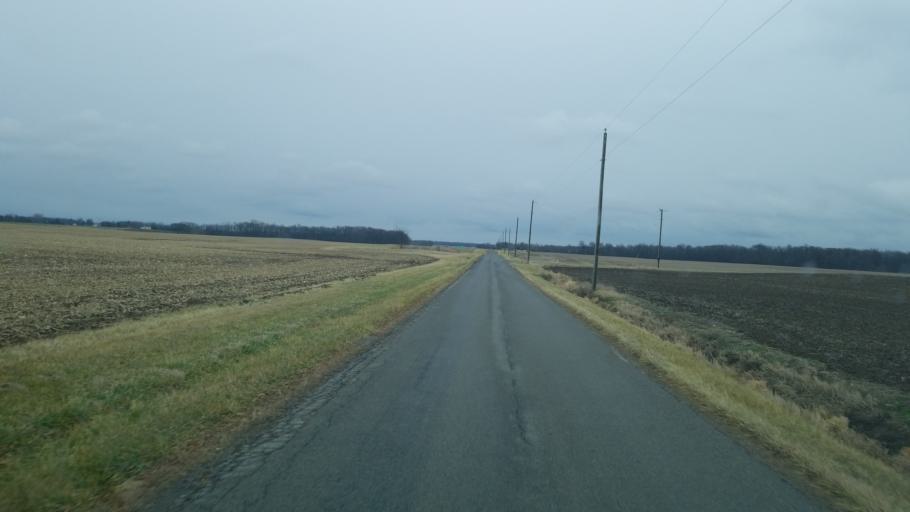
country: US
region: Ohio
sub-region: Union County
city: Marysville
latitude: 40.3094
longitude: -83.3154
